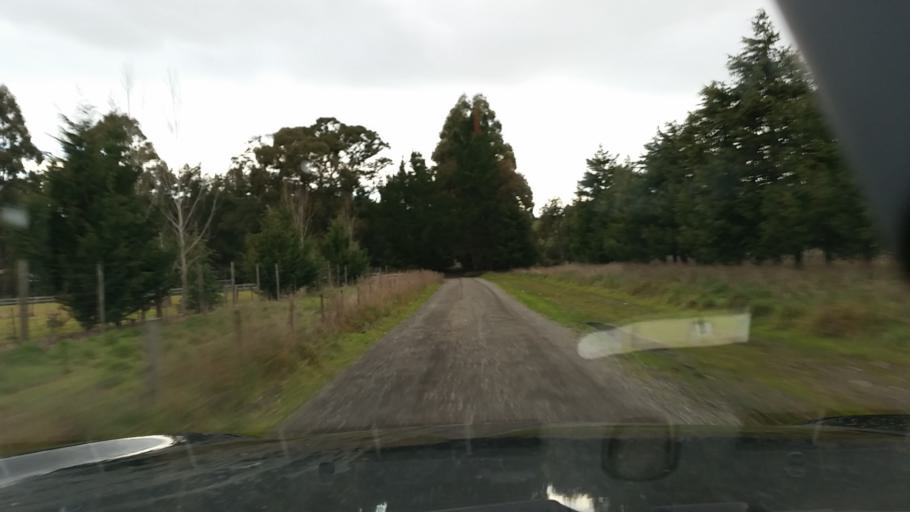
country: NZ
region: Marlborough
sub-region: Marlborough District
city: Blenheim
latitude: -41.5347
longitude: 173.6131
